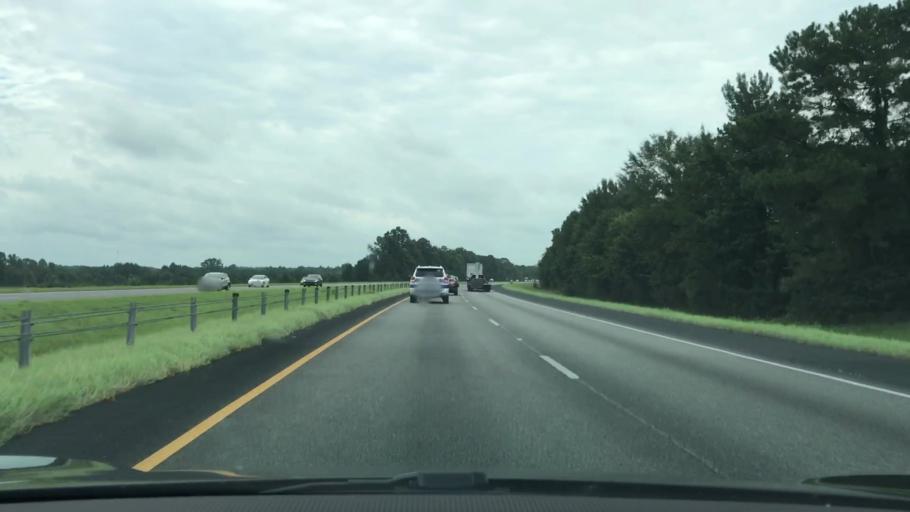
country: US
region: Alabama
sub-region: Elmore County
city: Tallassee
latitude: 32.4242
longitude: -85.9260
